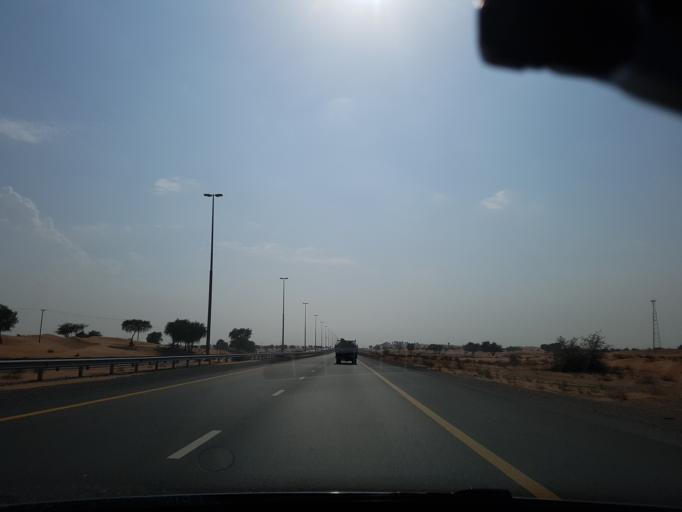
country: AE
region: Umm al Qaywayn
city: Umm al Qaywayn
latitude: 25.5221
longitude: 55.7552
